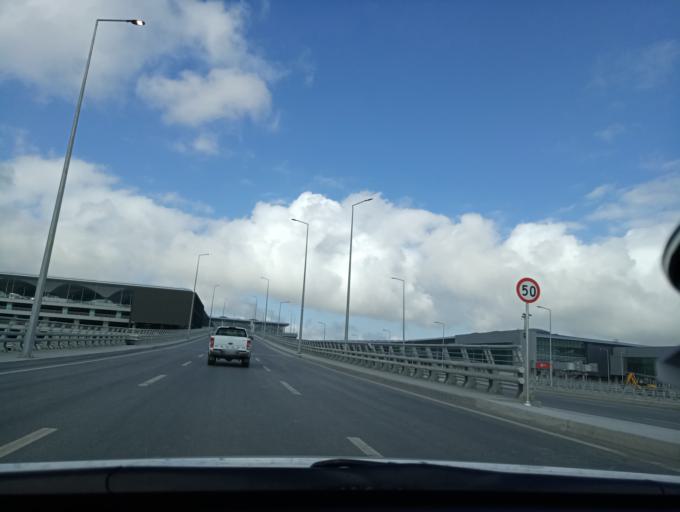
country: TR
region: Istanbul
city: Durusu
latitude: 41.2556
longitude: 28.7465
